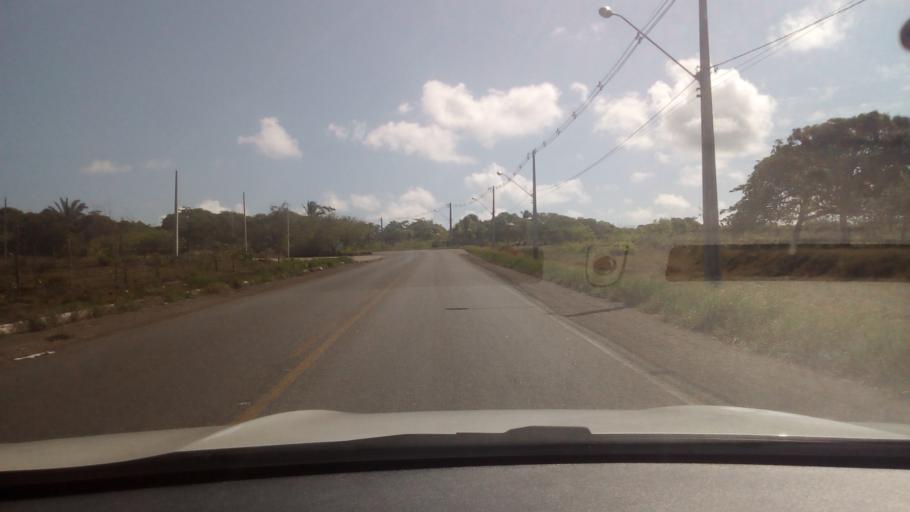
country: BR
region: Paraiba
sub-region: Joao Pessoa
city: Joao Pessoa
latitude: -7.2016
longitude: -34.8252
